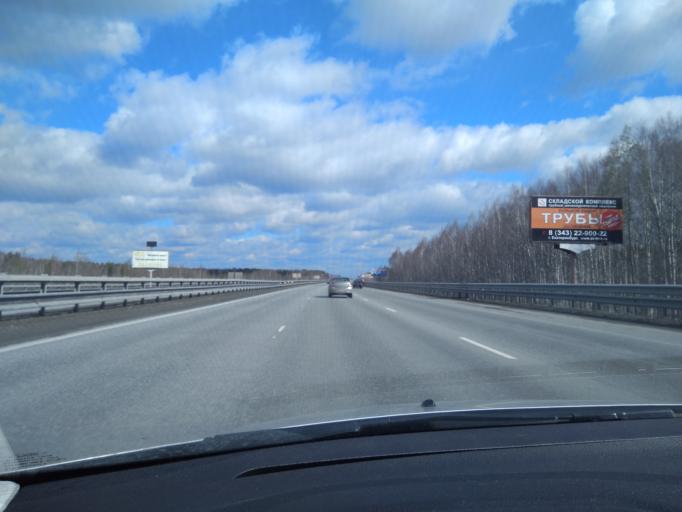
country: RU
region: Sverdlovsk
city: Shuvakish
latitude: 56.9181
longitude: 60.5083
